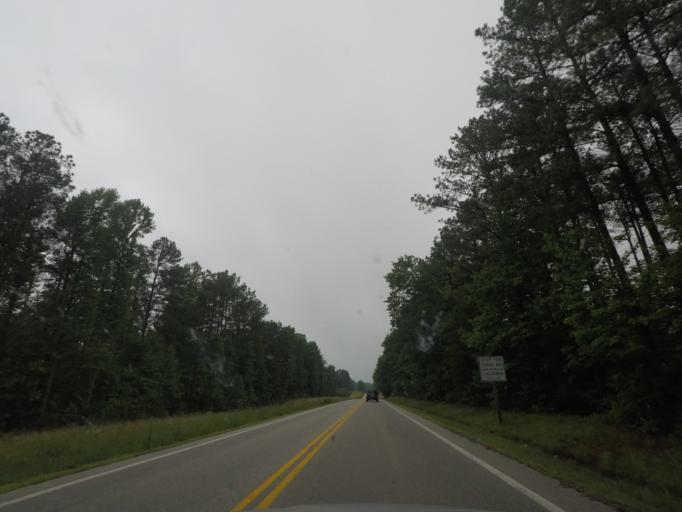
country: US
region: Virginia
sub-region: Prince Edward County
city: Hampden Sydney
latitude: 37.0888
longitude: -78.4747
